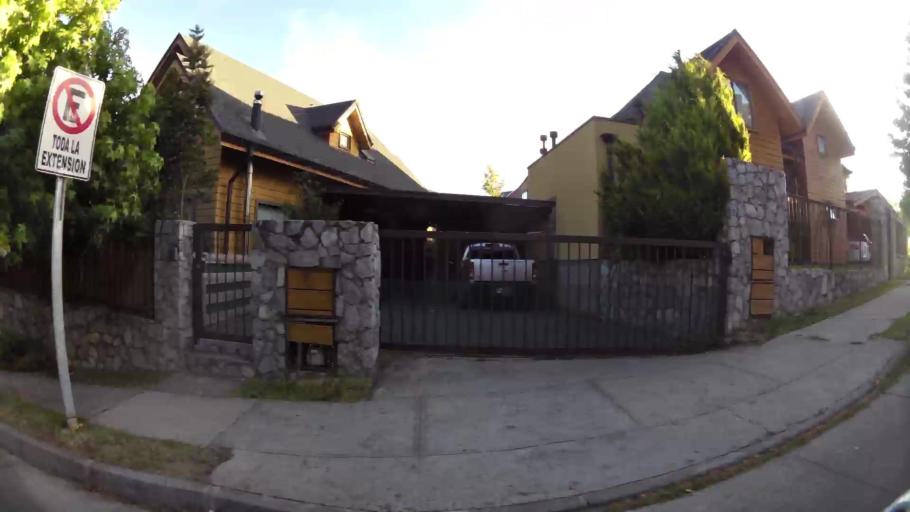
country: CL
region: Biobio
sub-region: Provincia de Concepcion
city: Concepcion
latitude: -36.8577
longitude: -73.0995
